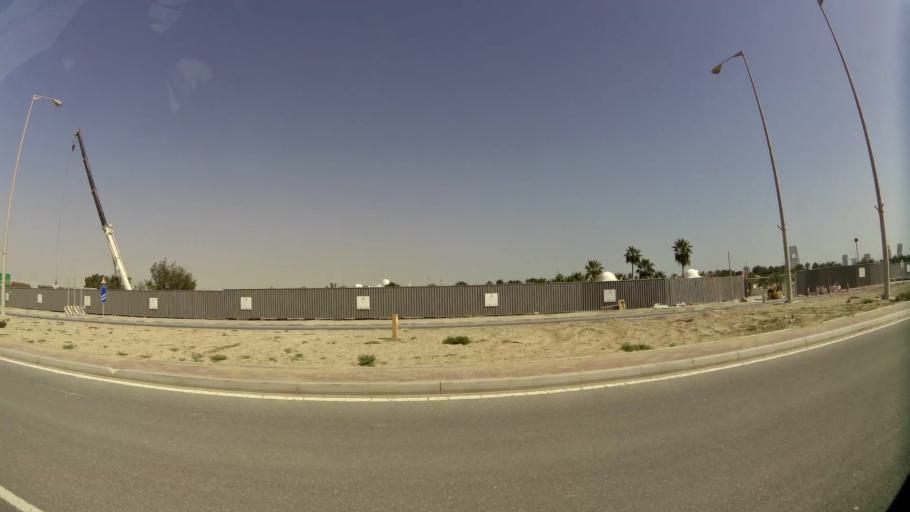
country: QA
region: Baladiyat ad Dawhah
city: Doha
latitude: 25.3771
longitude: 51.5030
